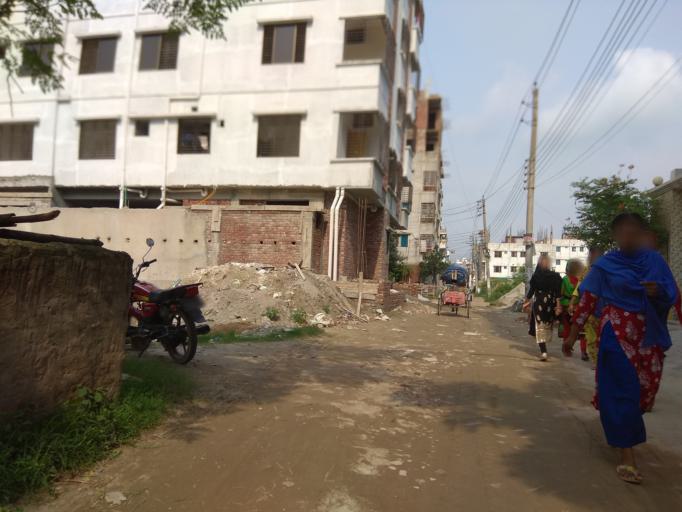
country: BD
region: Dhaka
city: Tungi
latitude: 23.8312
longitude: 90.3552
